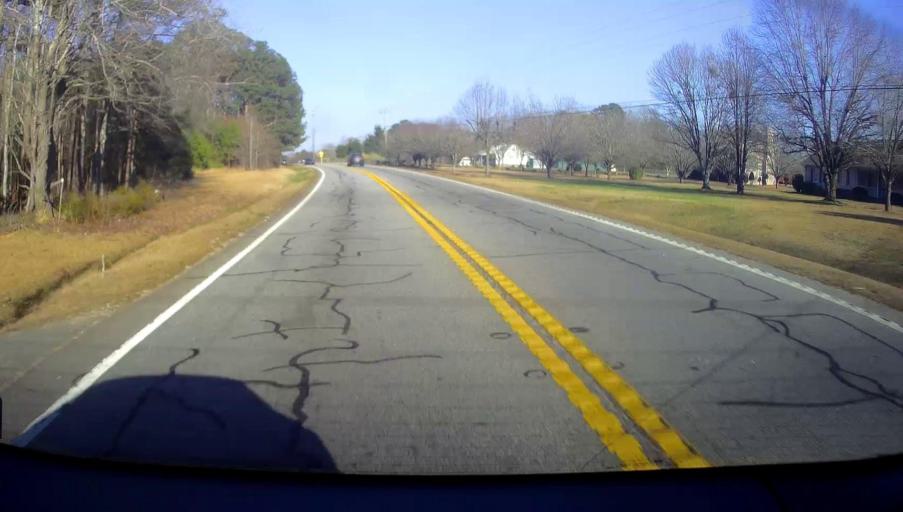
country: US
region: Georgia
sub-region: Henry County
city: Hampton
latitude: 33.4190
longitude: -84.2311
